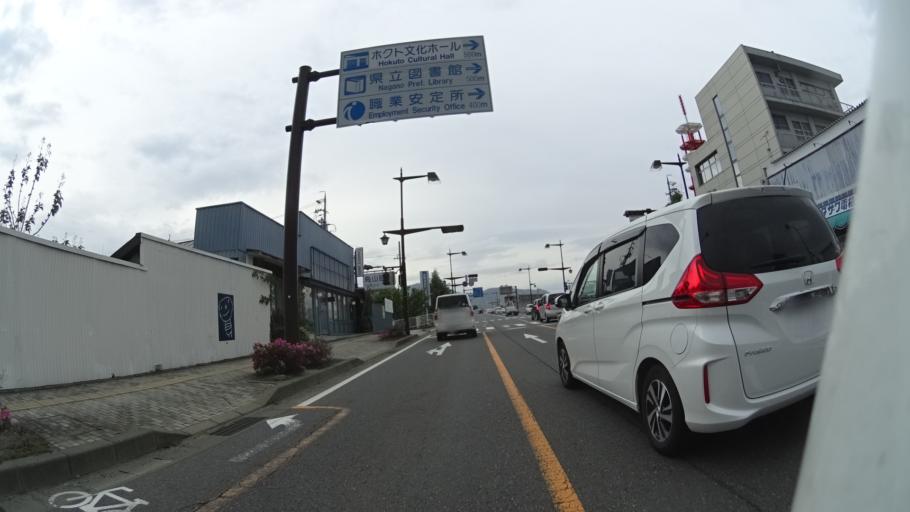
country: JP
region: Nagano
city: Nagano-shi
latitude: 36.6371
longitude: 138.1818
